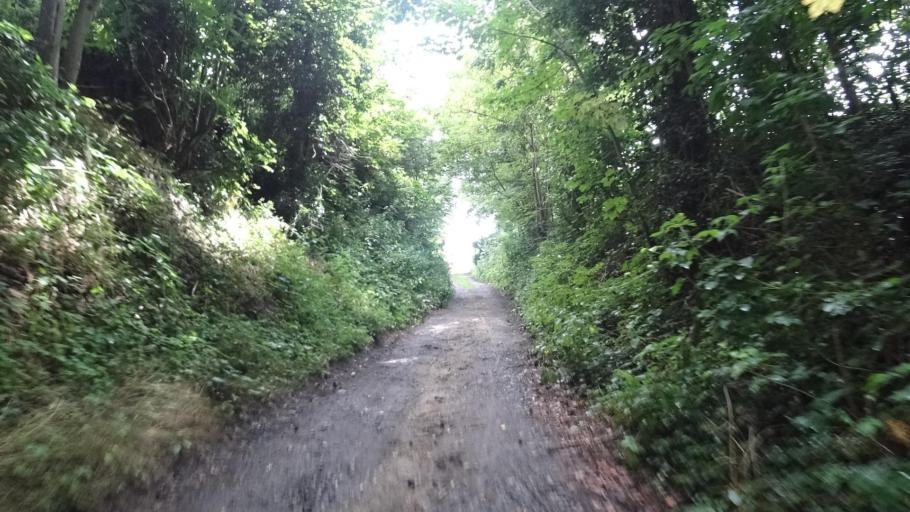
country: BE
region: Wallonia
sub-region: Province du Brabant Wallon
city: Villers-la-Ville
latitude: 50.5633
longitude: 4.5011
